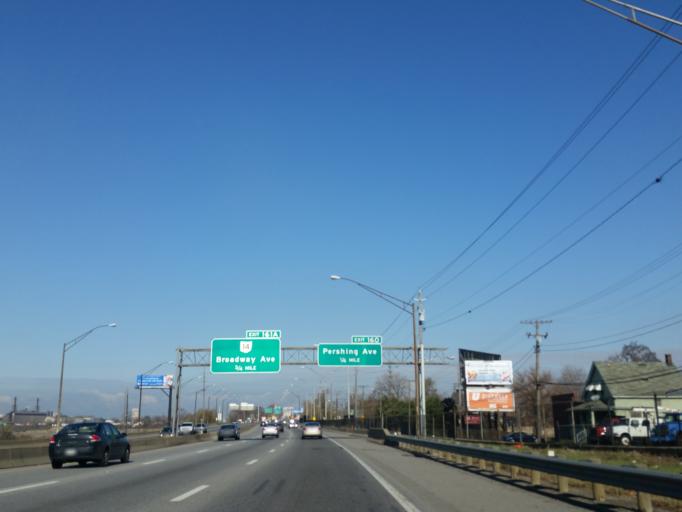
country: US
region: Ohio
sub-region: Cuyahoga County
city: Newburgh Heights
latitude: 41.4610
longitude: -81.6569
